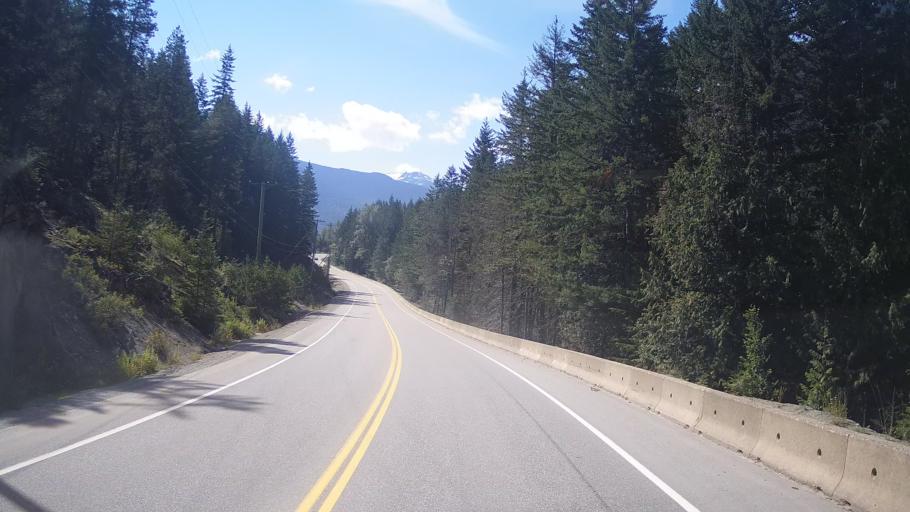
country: CA
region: British Columbia
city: Pemberton
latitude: 50.2173
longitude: -122.8854
